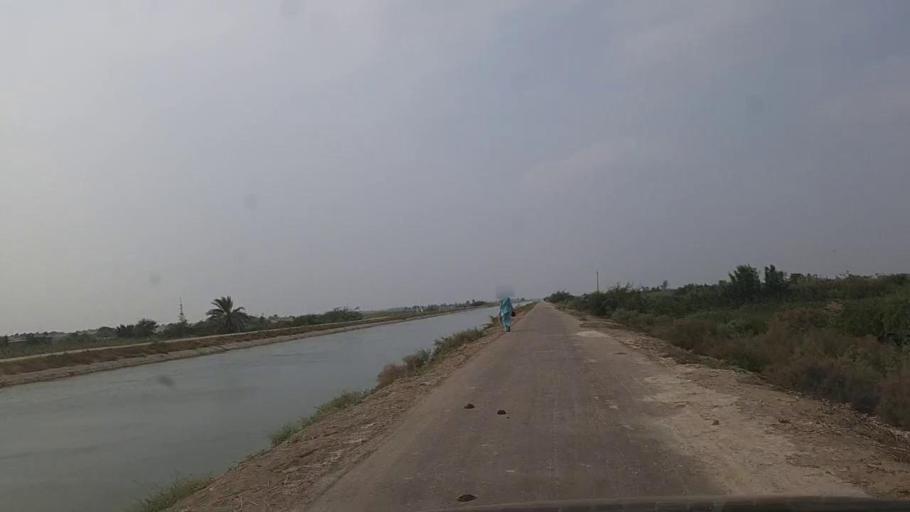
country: PK
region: Sindh
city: Thatta
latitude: 24.8034
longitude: 67.8989
